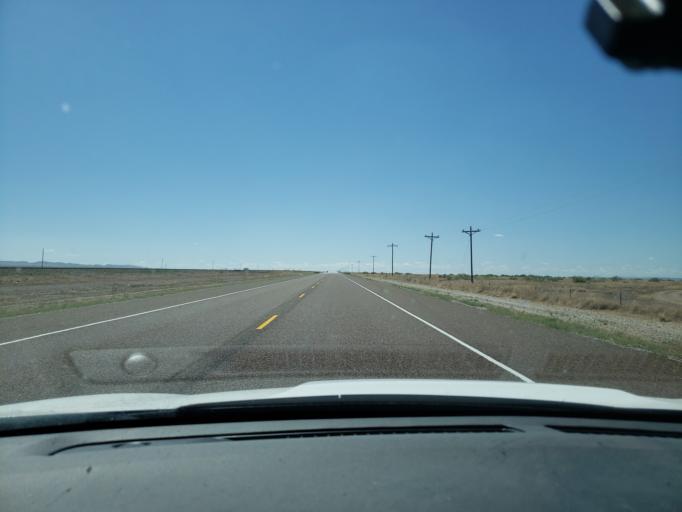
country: US
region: Texas
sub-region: Presidio County
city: Marfa
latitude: 30.5385
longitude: -104.4360
